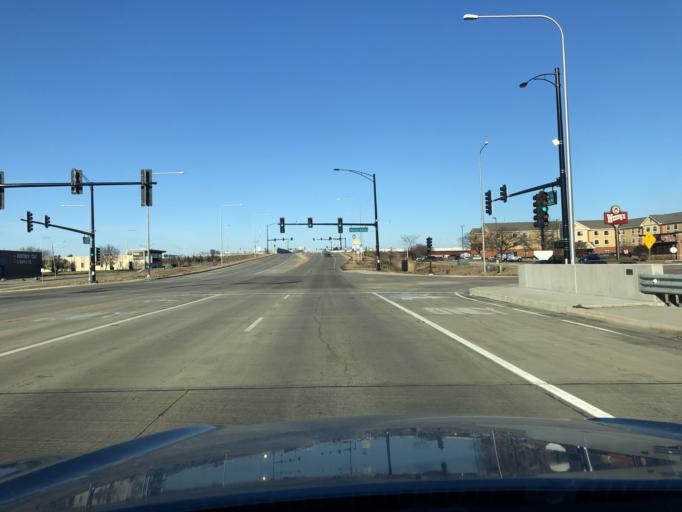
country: US
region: Illinois
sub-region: DuPage County
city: Itasca
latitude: 41.9844
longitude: -88.0314
